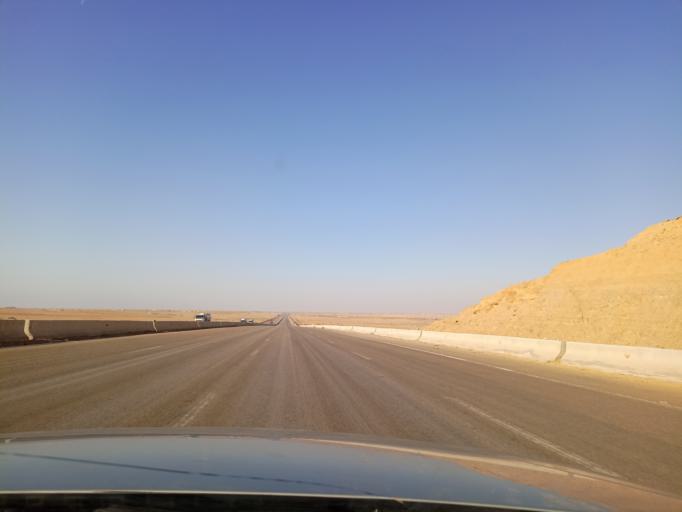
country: EG
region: Muhafazat al Fayyum
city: Tamiyah
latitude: 29.6153
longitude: 30.9311
